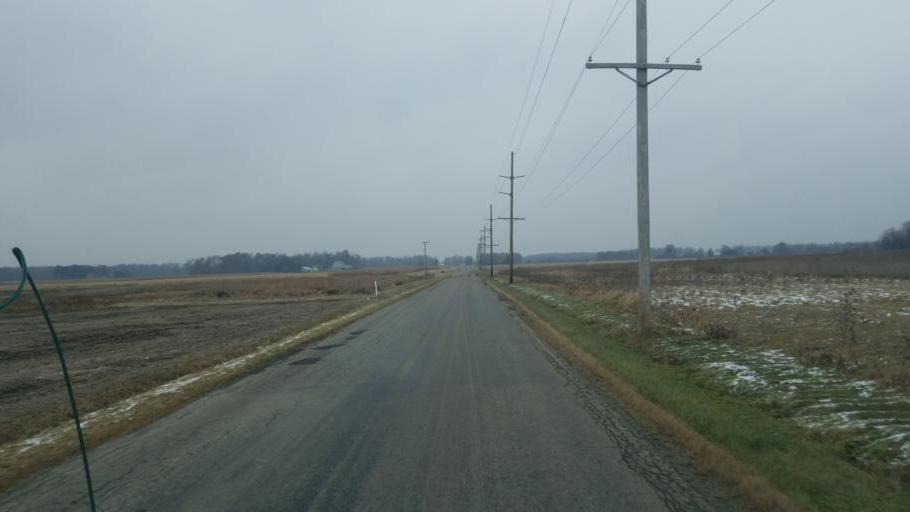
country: US
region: Ohio
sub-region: Richland County
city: Shelby
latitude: 40.9213
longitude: -82.6860
